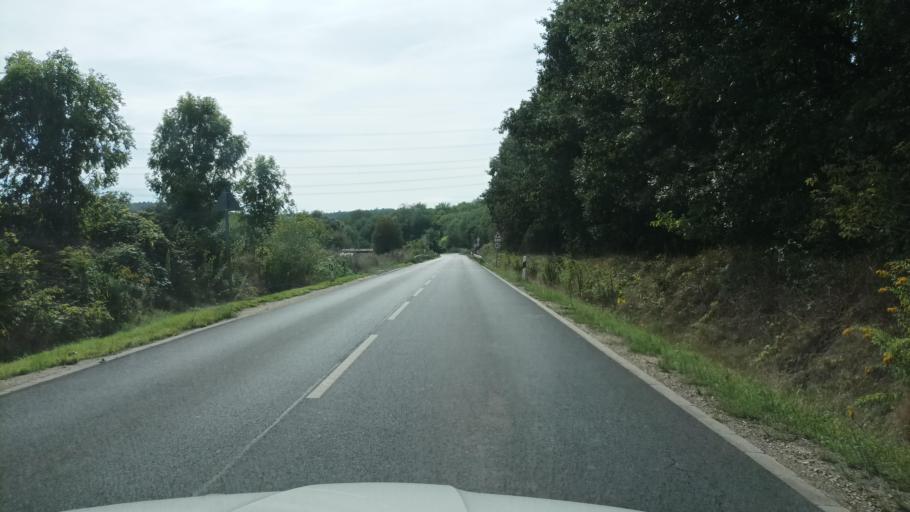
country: HU
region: Pest
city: Pecel
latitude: 47.5025
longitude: 19.3714
